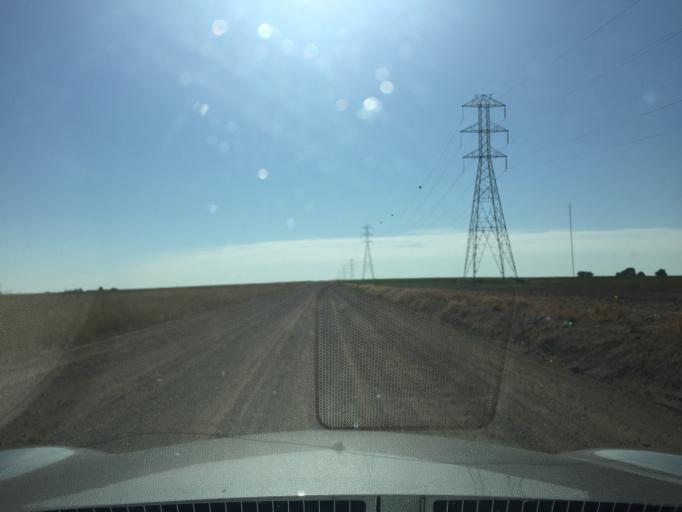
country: US
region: Colorado
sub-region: Boulder County
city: Erie
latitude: 40.0583
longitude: -105.0299
